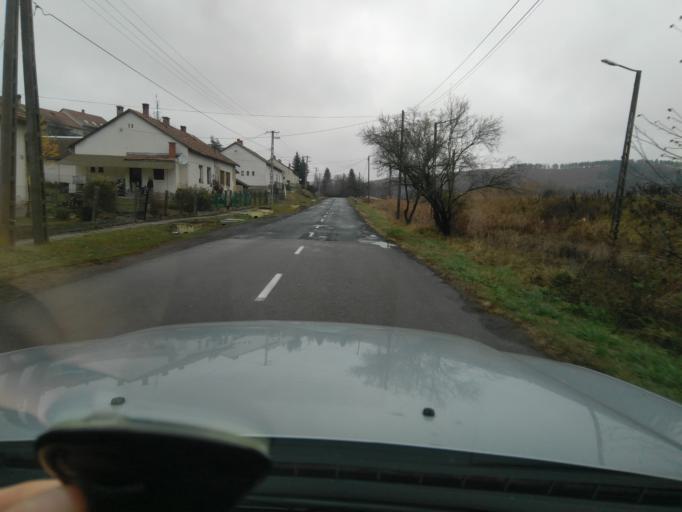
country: HU
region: Nograd
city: Kazar
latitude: 48.0253
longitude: 19.8681
